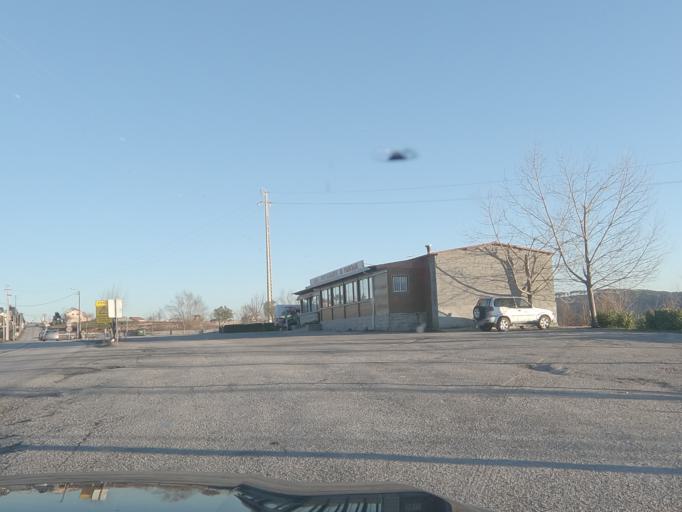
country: PT
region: Vila Real
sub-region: Ribeira de Pena
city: Ribeira de Pena
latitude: 41.4966
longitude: -7.7300
